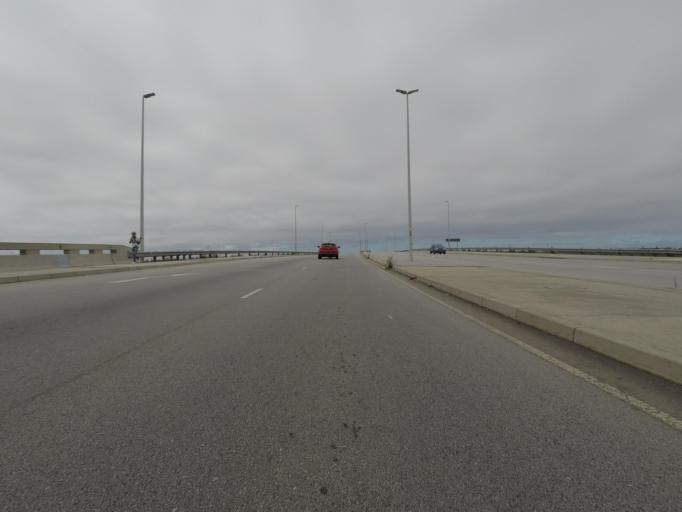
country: ZA
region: Eastern Cape
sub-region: Nelson Mandela Bay Metropolitan Municipality
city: Port Elizabeth
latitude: -33.9487
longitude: 25.4646
